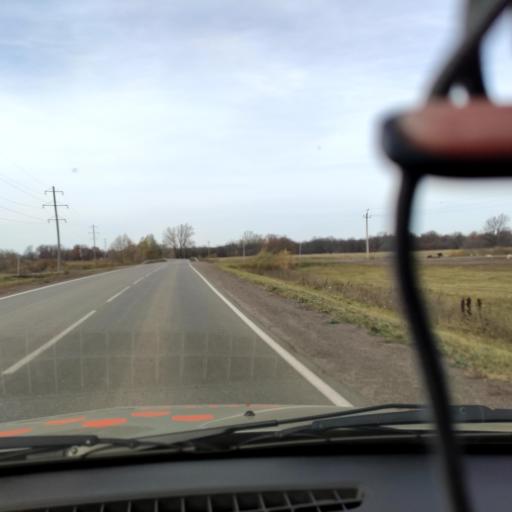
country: RU
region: Bashkortostan
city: Kabakovo
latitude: 54.5620
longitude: 55.9999
